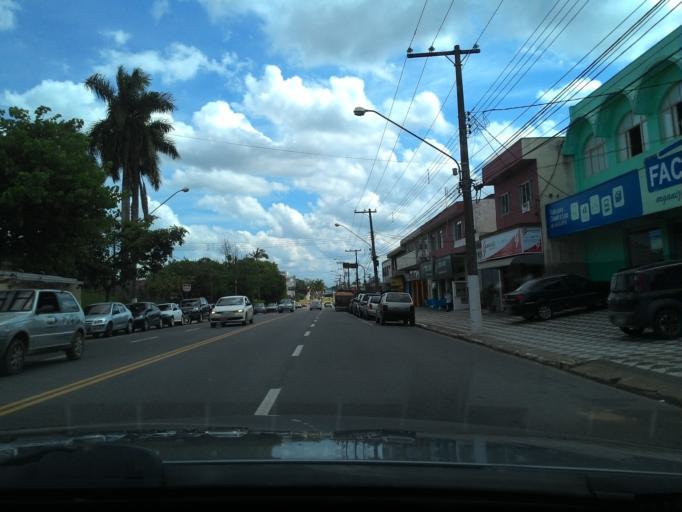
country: BR
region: Sao Paulo
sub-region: Registro
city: Registro
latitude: -24.5000
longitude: -47.8522
